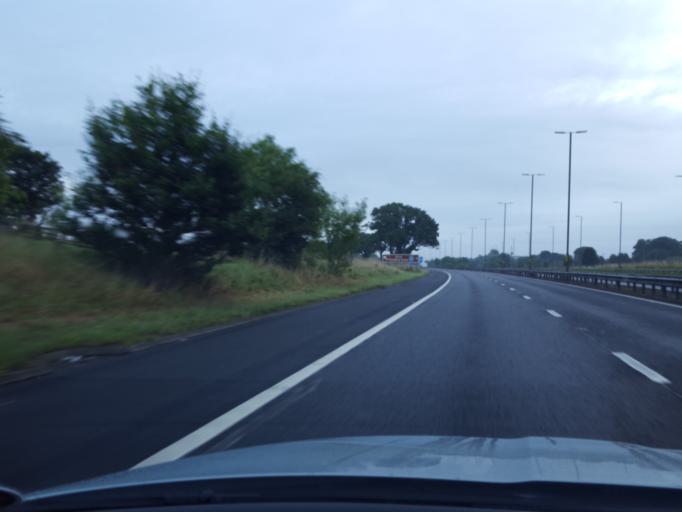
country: GB
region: Scotland
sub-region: Edinburgh
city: Newbridge
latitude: 55.9251
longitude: -3.4222
